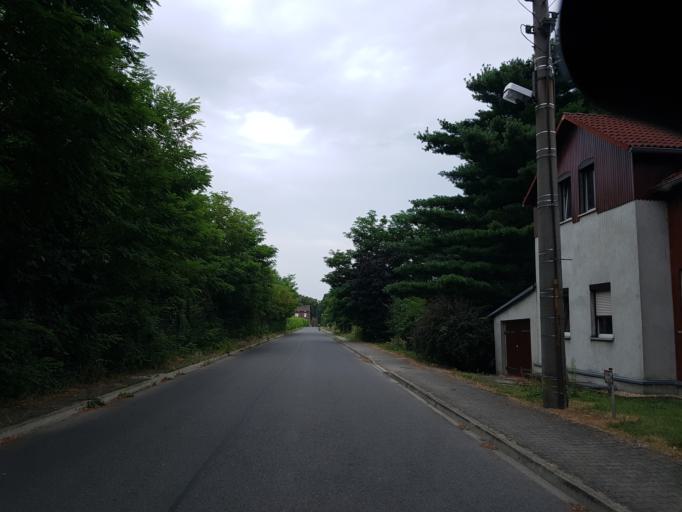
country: DE
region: Brandenburg
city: Sallgast
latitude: 51.5632
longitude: 13.8864
